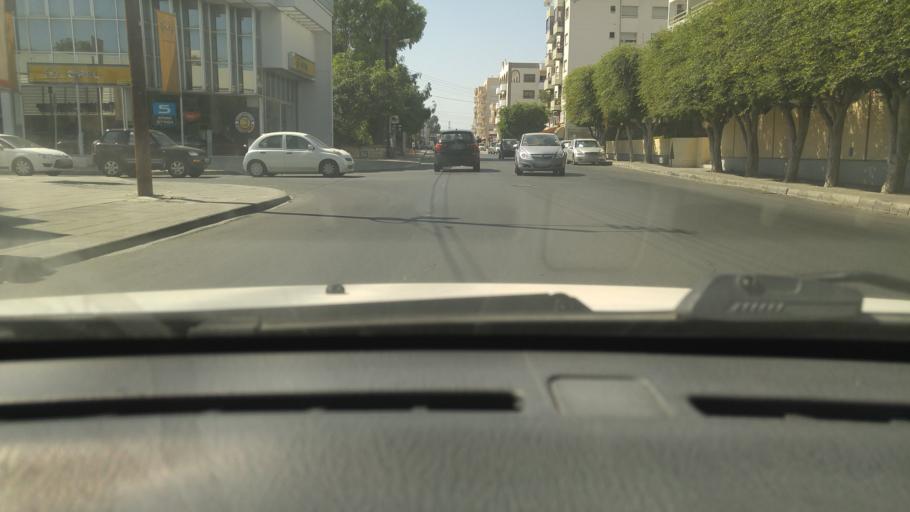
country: CY
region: Limassol
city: Limassol
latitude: 34.6744
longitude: 33.0263
